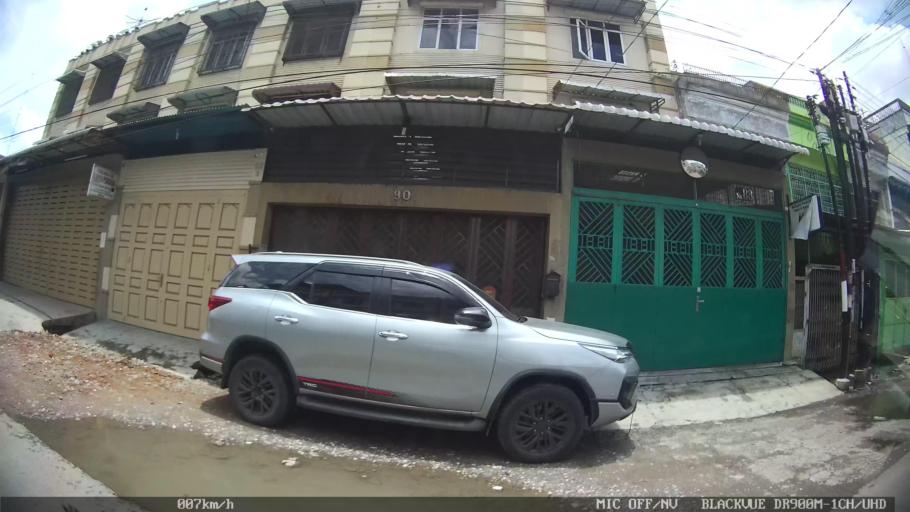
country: ID
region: North Sumatra
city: Medan
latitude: 3.5947
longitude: 98.7113
